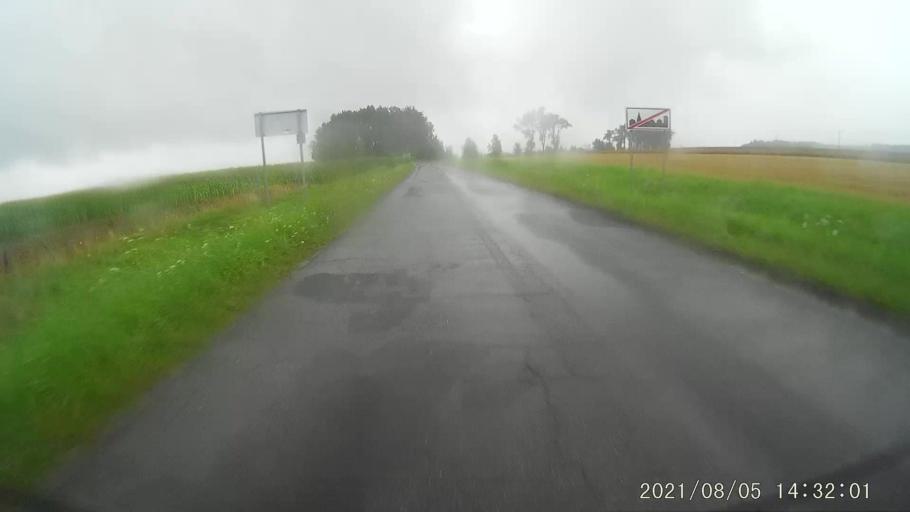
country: PL
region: Opole Voivodeship
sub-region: Powiat nyski
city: Korfantow
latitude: 50.4698
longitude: 17.5529
